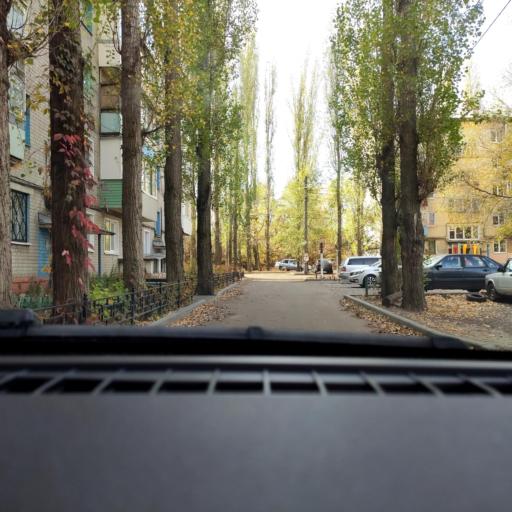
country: RU
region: Voronezj
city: Maslovka
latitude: 51.6116
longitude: 39.2527
